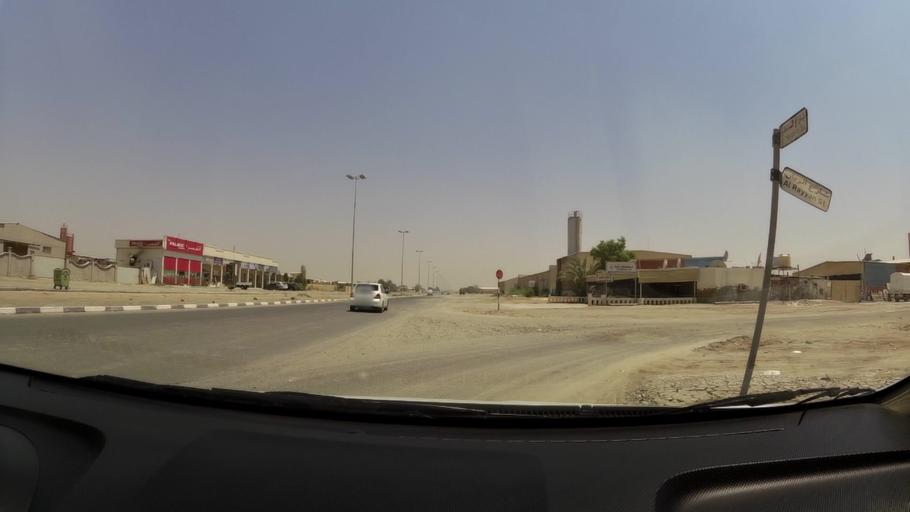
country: AE
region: Umm al Qaywayn
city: Umm al Qaywayn
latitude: 25.5088
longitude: 55.5588
